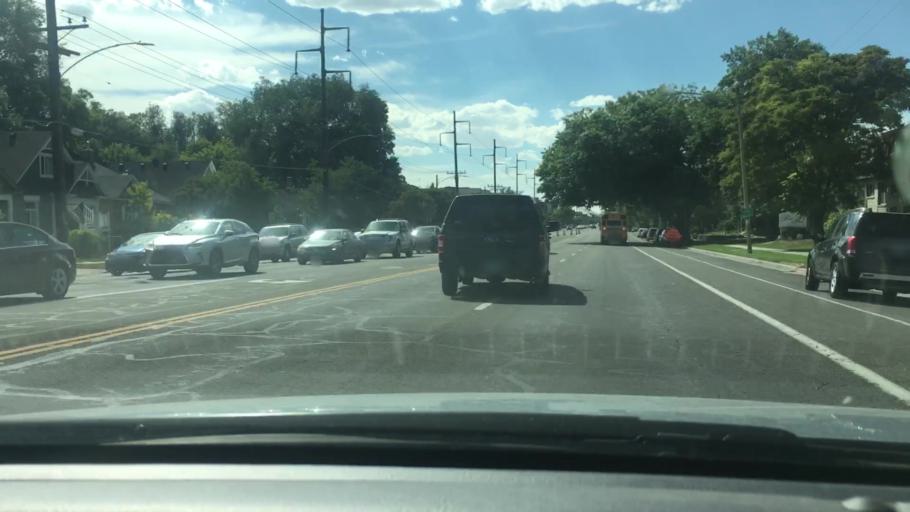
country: US
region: Utah
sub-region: Salt Lake County
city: Salt Lake City
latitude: 40.7520
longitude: -111.8801
